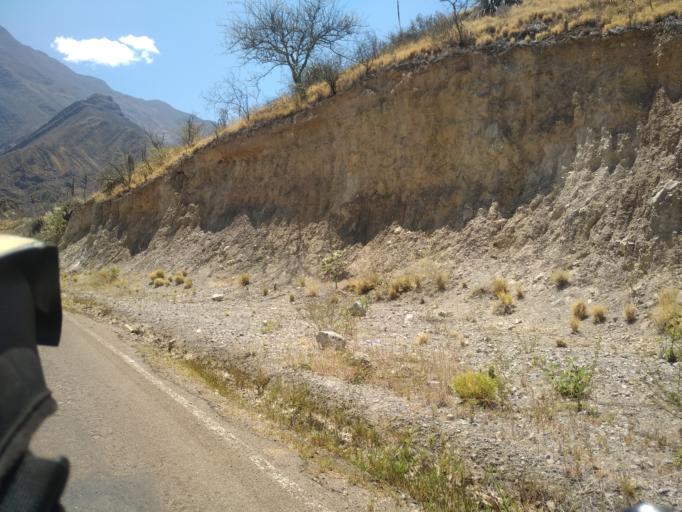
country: PE
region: Amazonas
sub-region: Provincia de Chachapoyas
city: Balsas
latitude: -6.8472
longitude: -78.0414
